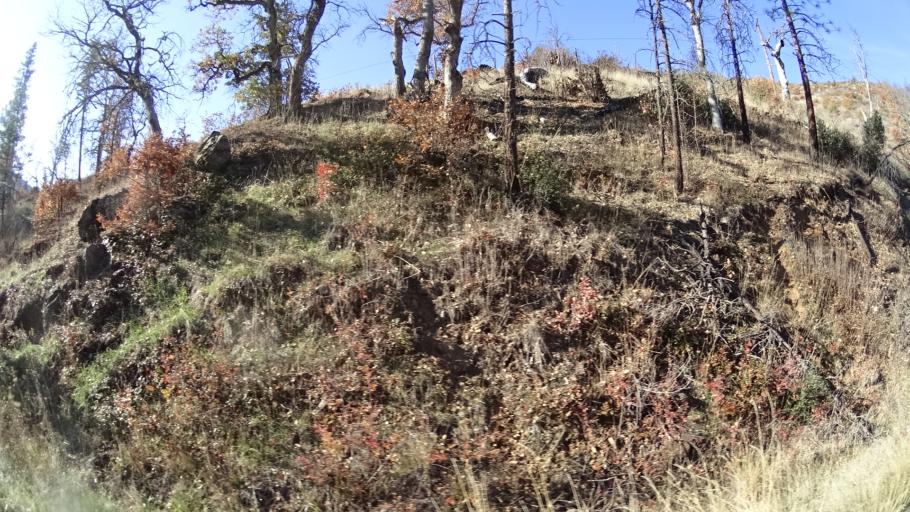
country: US
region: California
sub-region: Siskiyou County
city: Yreka
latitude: 41.8726
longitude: -122.8186
